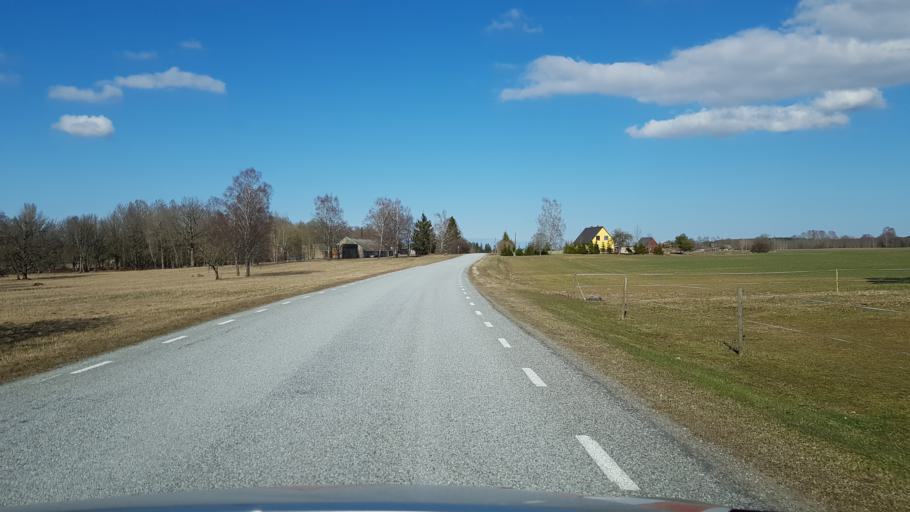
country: EE
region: Laeaene-Virumaa
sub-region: Rakvere linn
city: Rakvere
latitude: 59.3235
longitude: 26.2693
